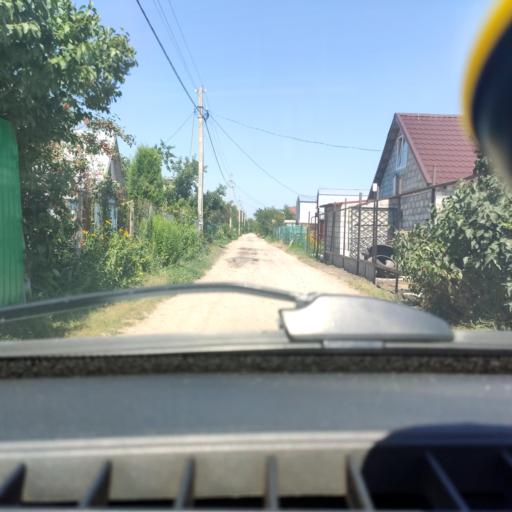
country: RU
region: Samara
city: Tol'yatti
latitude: 53.5951
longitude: 49.3046
